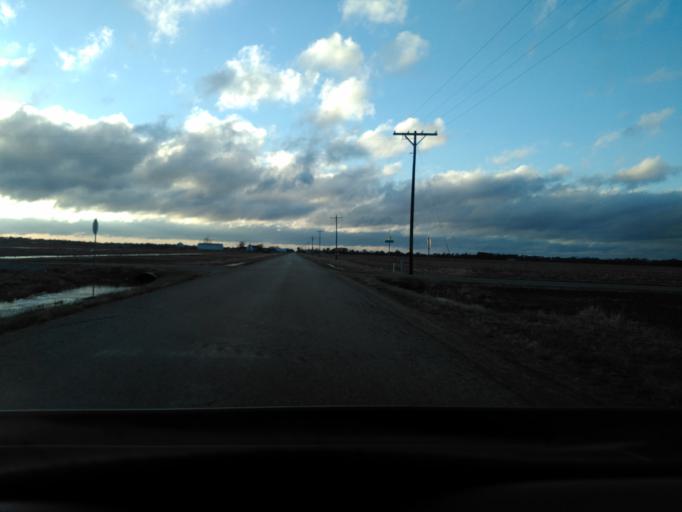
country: US
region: Illinois
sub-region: Effingham County
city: Altamont
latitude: 38.9577
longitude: -88.7298
